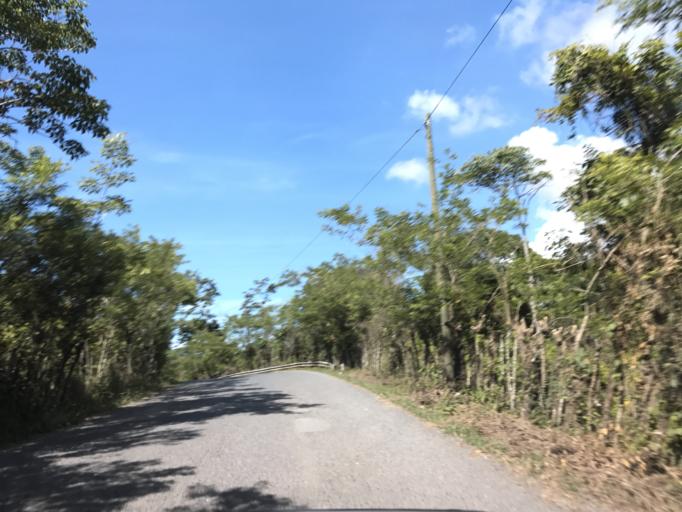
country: GT
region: Izabal
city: Morales
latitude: 15.6422
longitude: -89.0303
